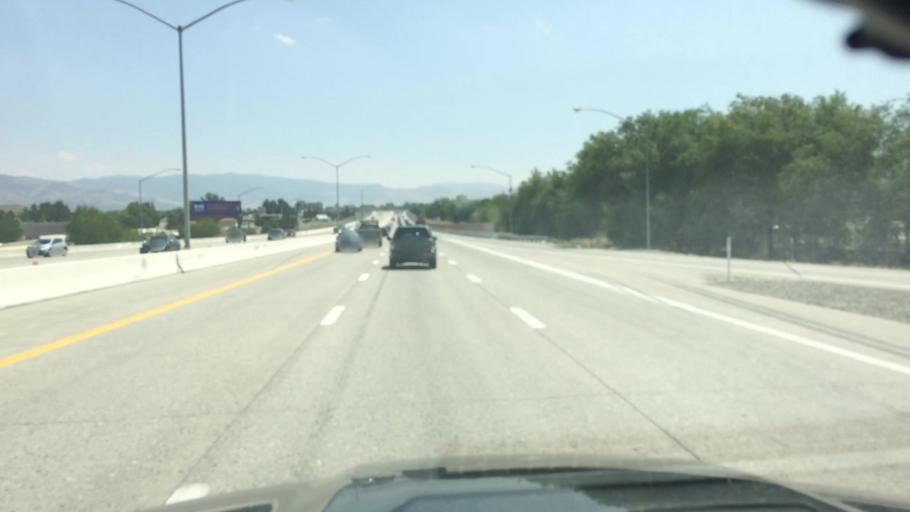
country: US
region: Nevada
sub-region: Washoe County
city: Reno
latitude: 39.4648
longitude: -119.7869
